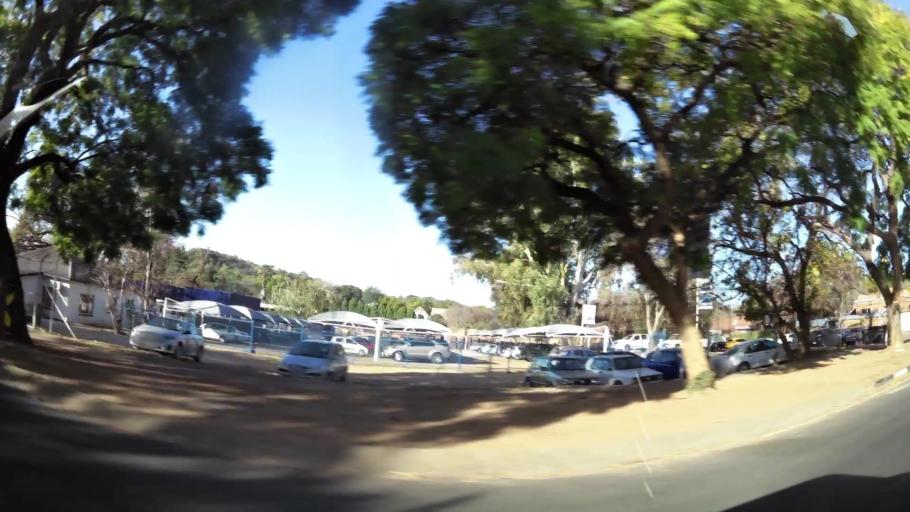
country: ZA
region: Gauteng
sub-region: City of Tshwane Metropolitan Municipality
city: Pretoria
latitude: -25.7291
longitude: 28.2153
